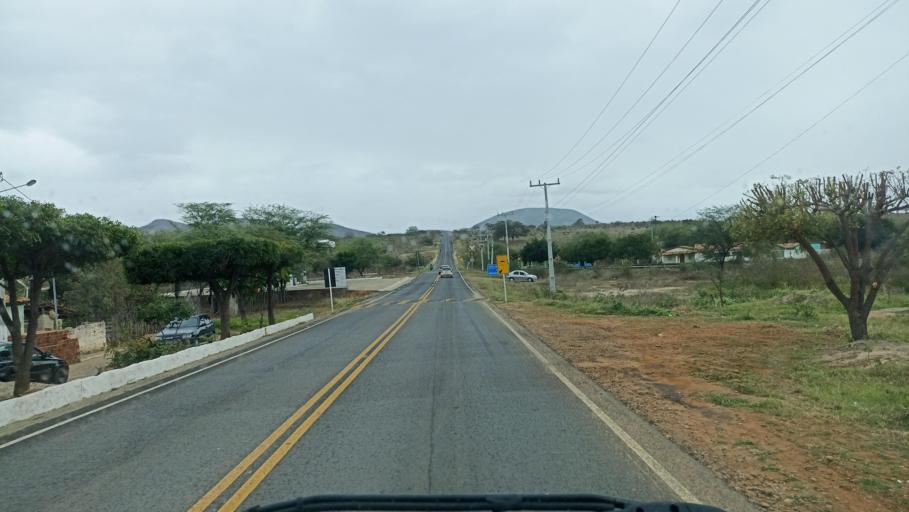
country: BR
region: Bahia
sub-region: Andarai
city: Vera Cruz
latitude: -13.0487
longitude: -40.7475
